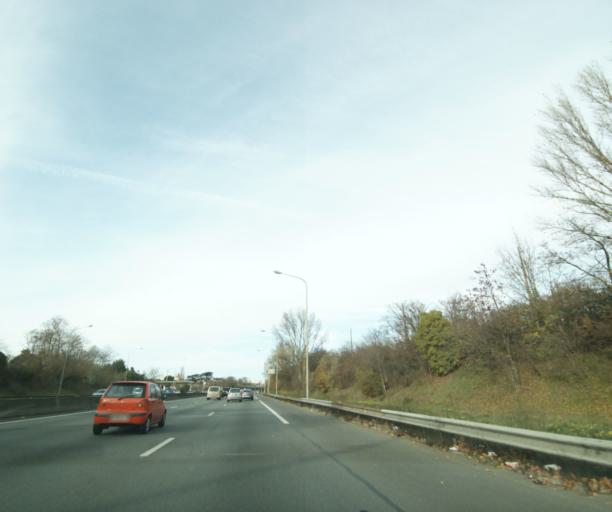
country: FR
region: Midi-Pyrenees
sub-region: Departement de la Haute-Garonne
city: Blagnac
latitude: 43.5924
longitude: 1.3987
